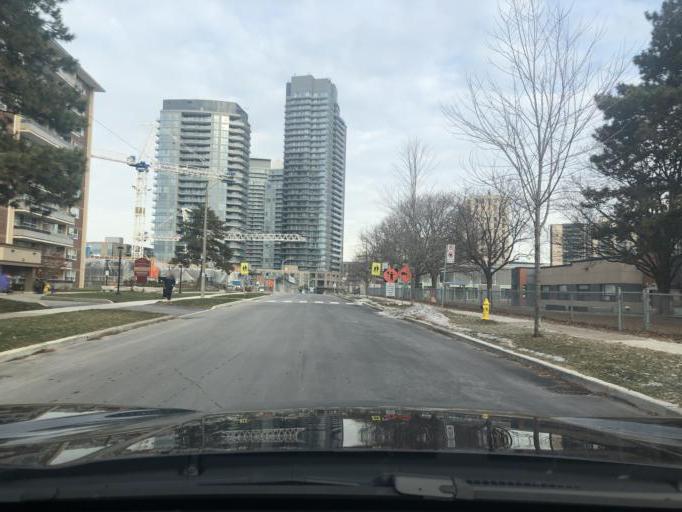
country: CA
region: Ontario
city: Willowdale
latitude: 43.7708
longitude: -79.3440
